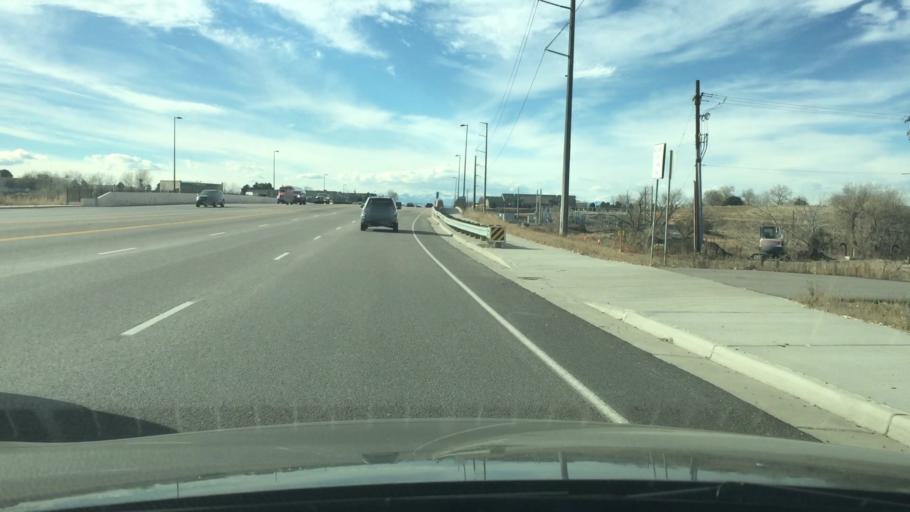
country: US
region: Colorado
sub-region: Arapahoe County
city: Dove Valley
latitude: 39.5951
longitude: -104.8111
